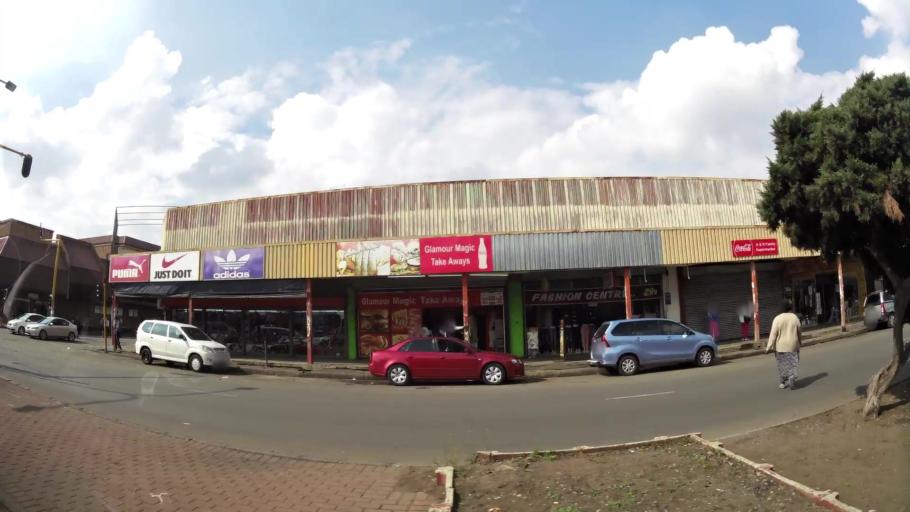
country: ZA
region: Gauteng
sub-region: Sedibeng District Municipality
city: Vereeniging
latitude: -26.6766
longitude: 27.9312
